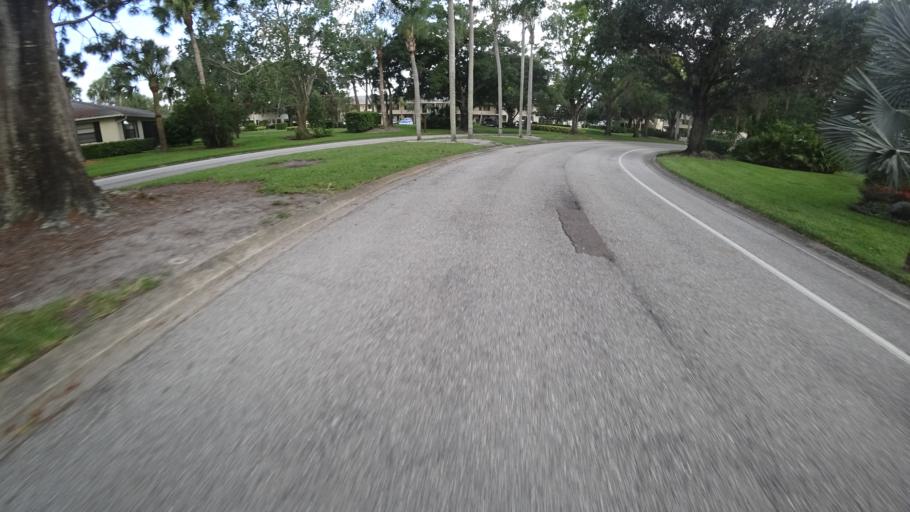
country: US
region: Florida
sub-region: Sarasota County
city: Desoto Lakes
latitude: 27.4164
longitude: -82.4933
